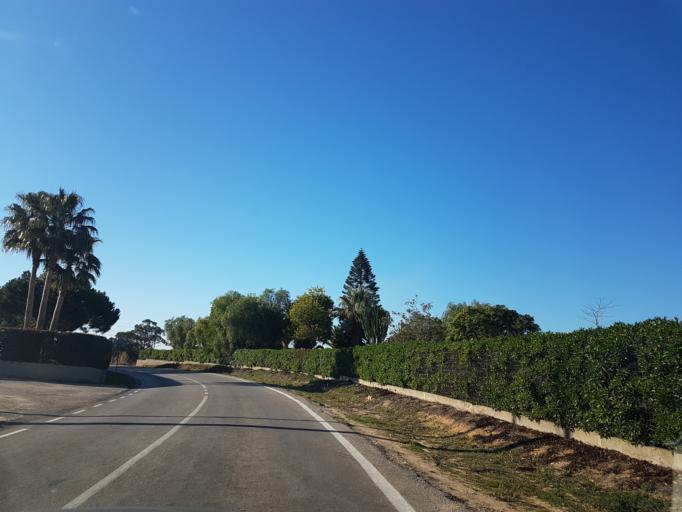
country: PT
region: Faro
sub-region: Lagoa
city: Carvoeiro
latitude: 37.1041
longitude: -8.4153
